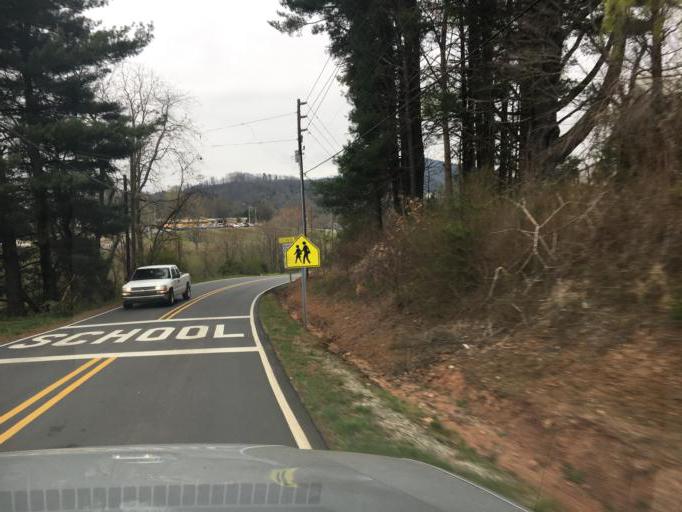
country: US
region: North Carolina
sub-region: Buncombe County
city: Woodfin
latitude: 35.6200
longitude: -82.6204
